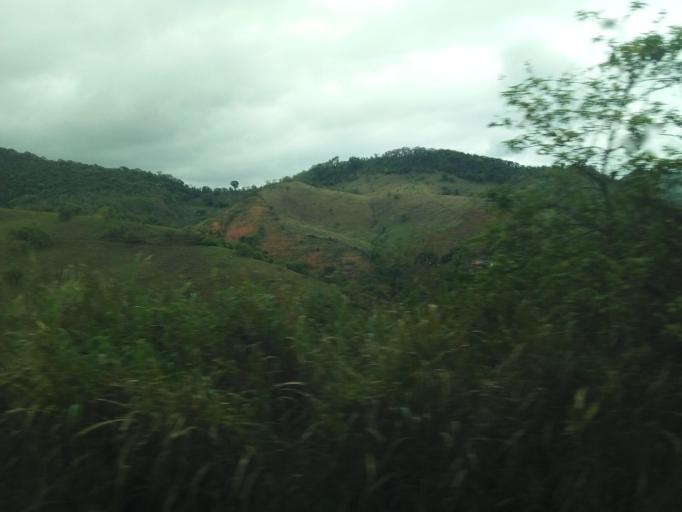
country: BR
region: Minas Gerais
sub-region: Nova Era
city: Nova Era
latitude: -19.6810
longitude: -42.9127
